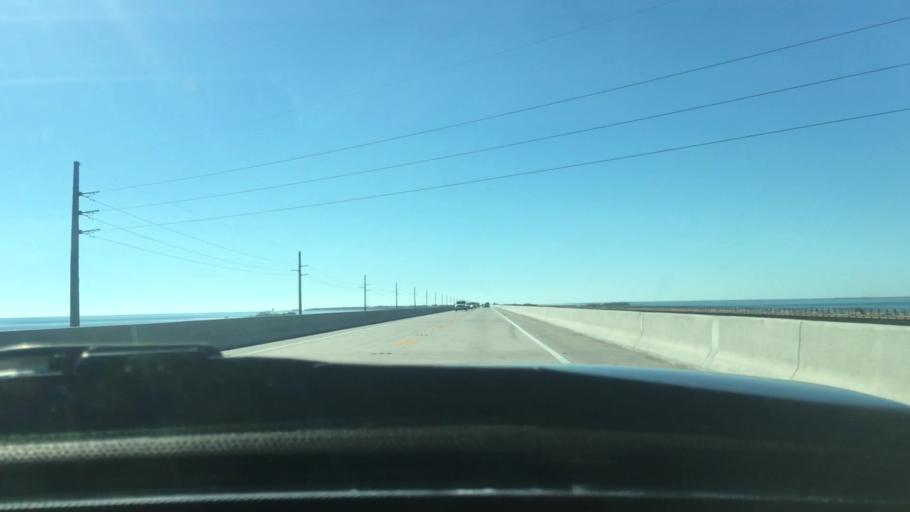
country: US
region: Florida
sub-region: Monroe County
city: Marathon
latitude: 24.6889
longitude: -81.2051
